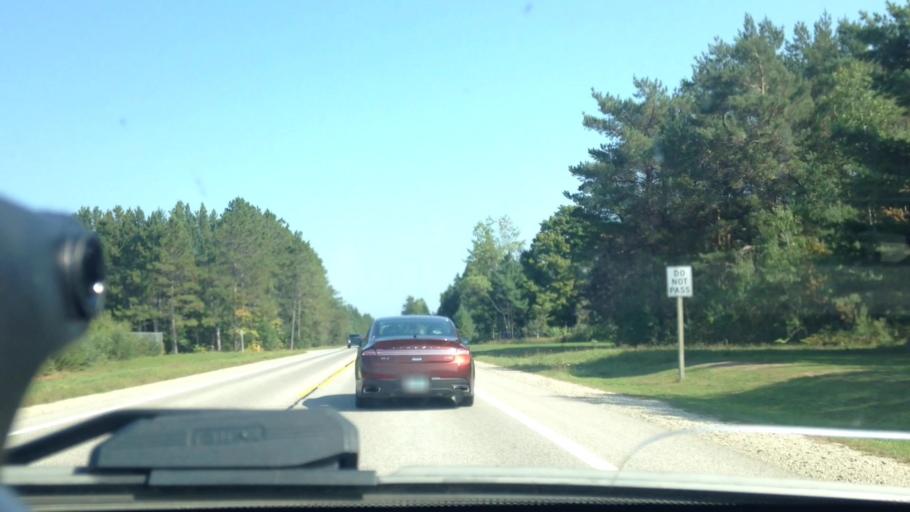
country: US
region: Michigan
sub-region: Luce County
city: Newberry
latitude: 46.3037
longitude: -85.4485
